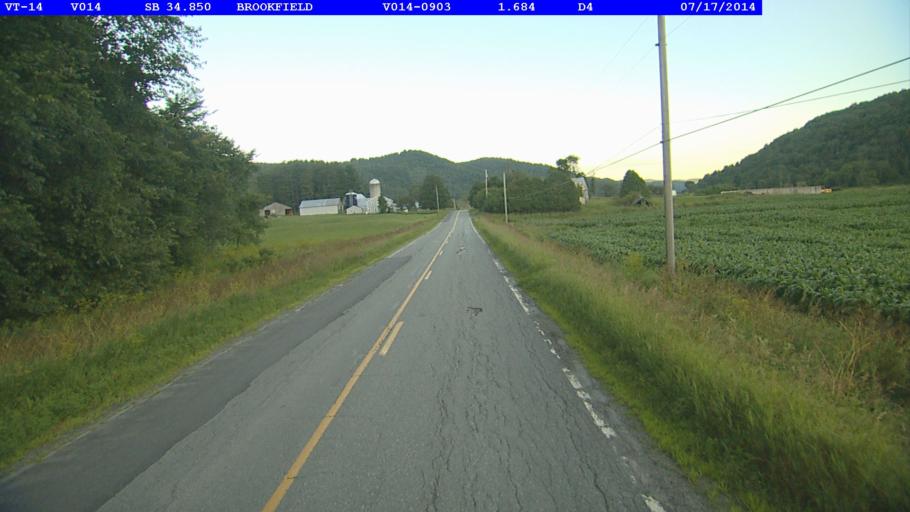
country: US
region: Vermont
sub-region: Orange County
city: Chelsea
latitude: 44.0021
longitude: -72.5626
